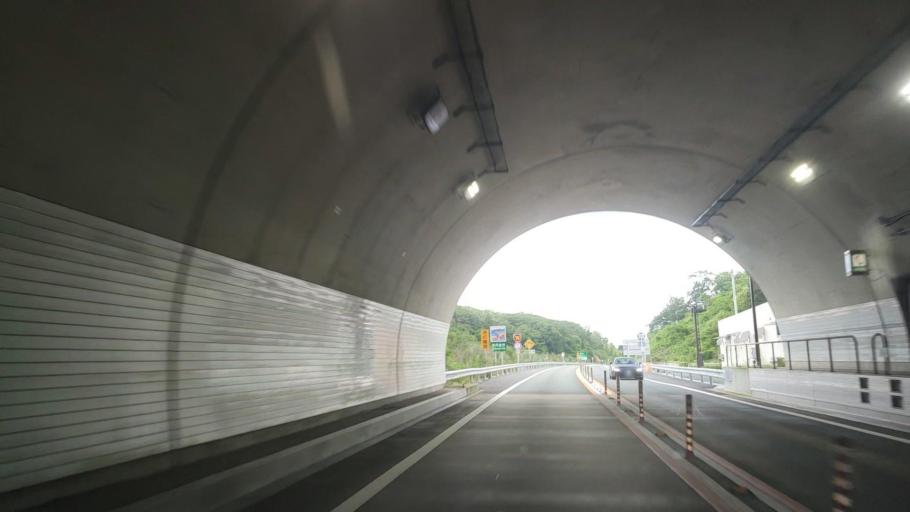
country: JP
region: Kyoto
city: Miyazu
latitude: 35.5661
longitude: 135.1207
